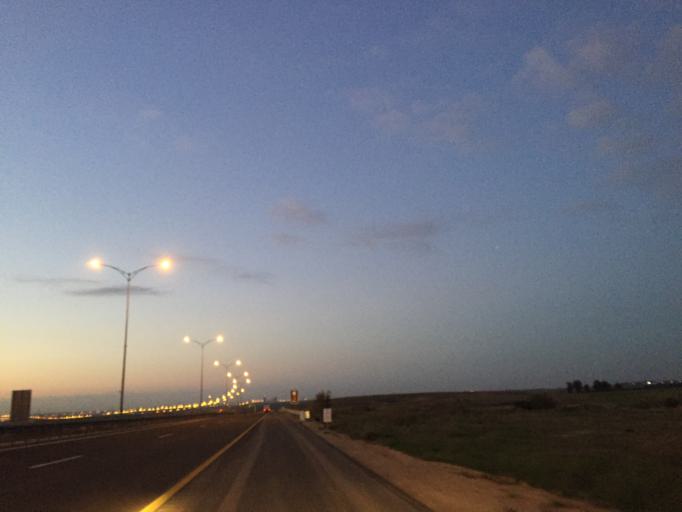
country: IL
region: Southern District
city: Lehavim
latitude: 31.3745
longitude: 34.8246
